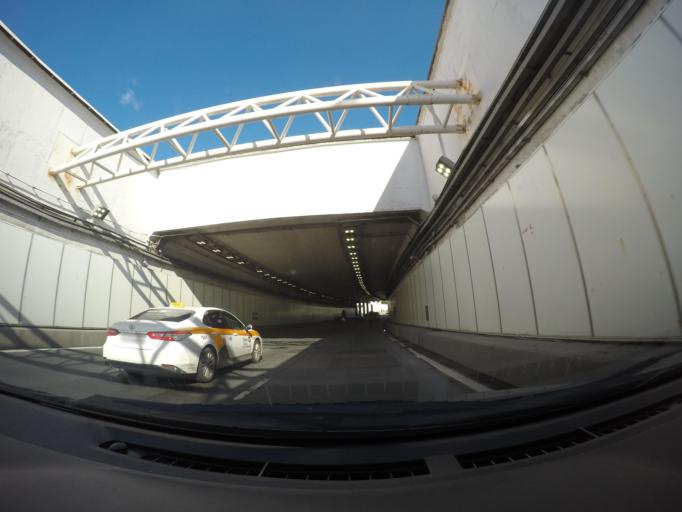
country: RU
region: Moscow
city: Sokol
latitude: 55.8063
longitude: 37.5102
